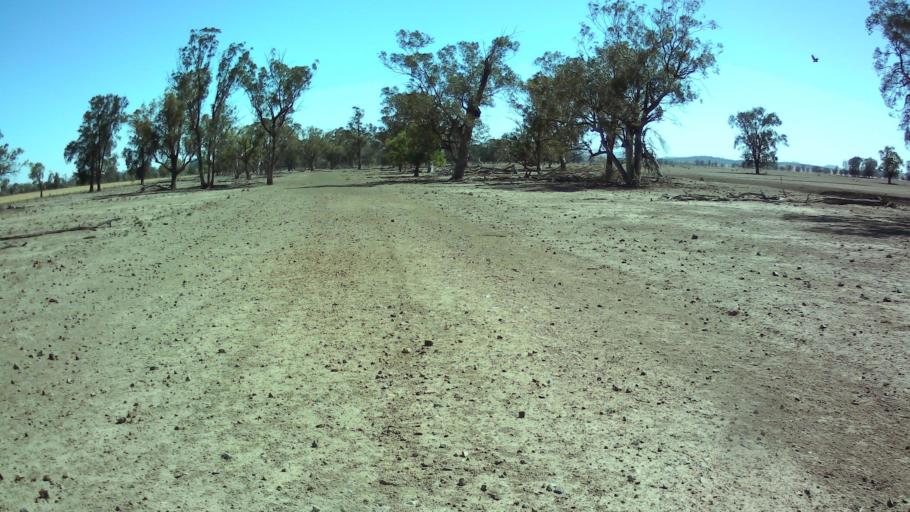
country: AU
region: New South Wales
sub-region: Bland
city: West Wyalong
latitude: -33.7679
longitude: 147.6574
